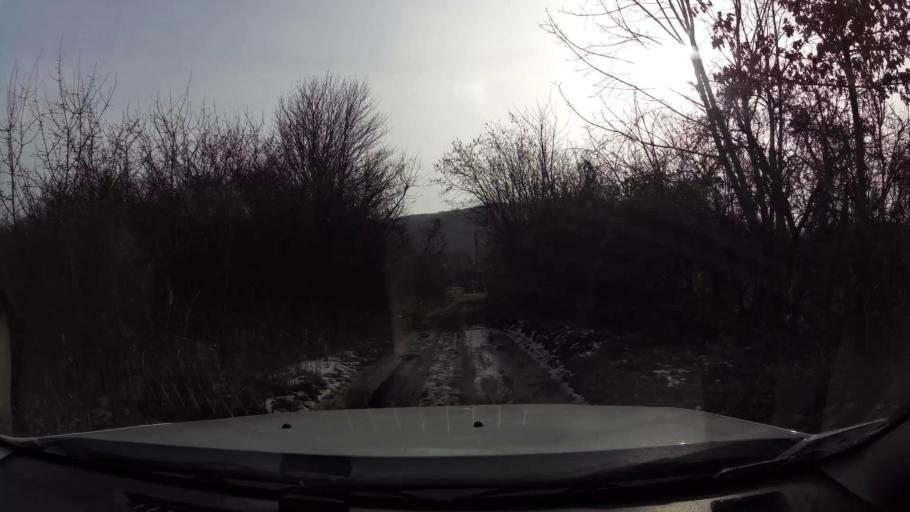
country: PL
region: West Pomeranian Voivodeship
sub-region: Powiat kamienski
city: Miedzyzdroje
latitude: 53.8807
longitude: 14.4481
